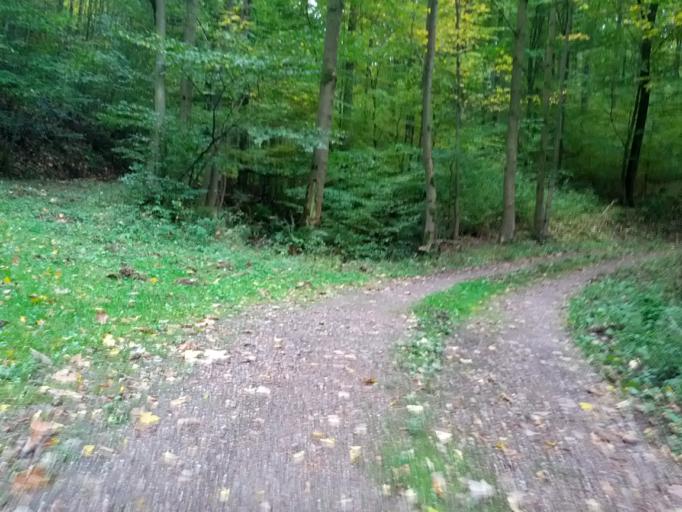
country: DE
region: Thuringia
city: Wolfsburg-Unkeroda
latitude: 50.9715
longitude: 10.2758
